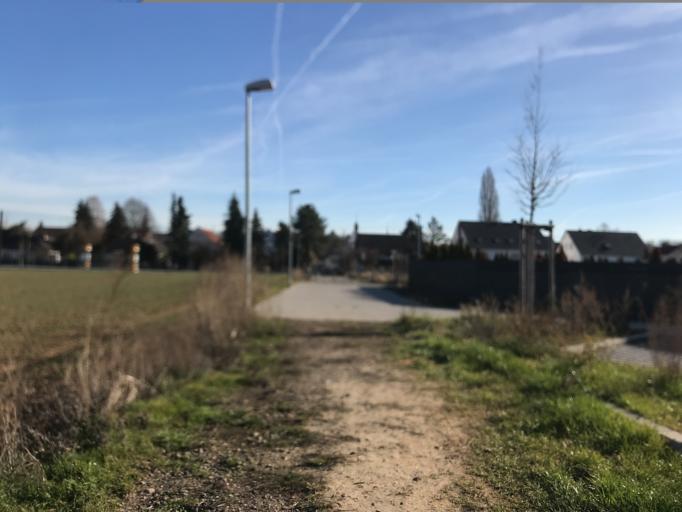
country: DE
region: Rheinland-Pfalz
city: Klein-Winternheim
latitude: 49.9633
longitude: 8.2262
